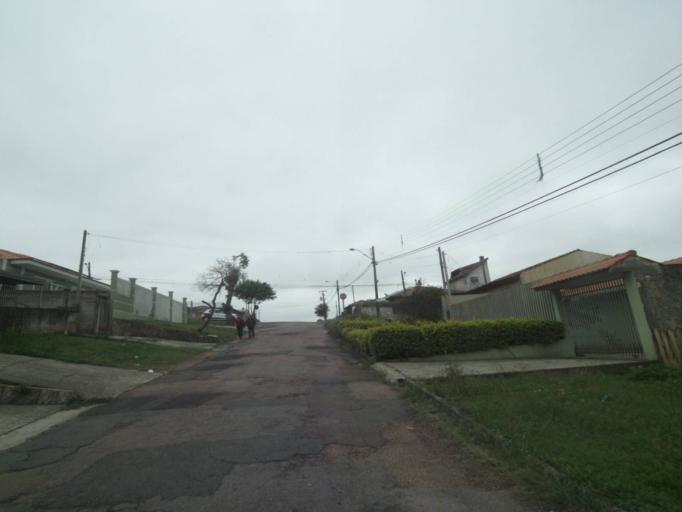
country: BR
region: Parana
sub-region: Sao Jose Dos Pinhais
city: Sao Jose dos Pinhais
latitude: -25.5416
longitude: -49.2869
